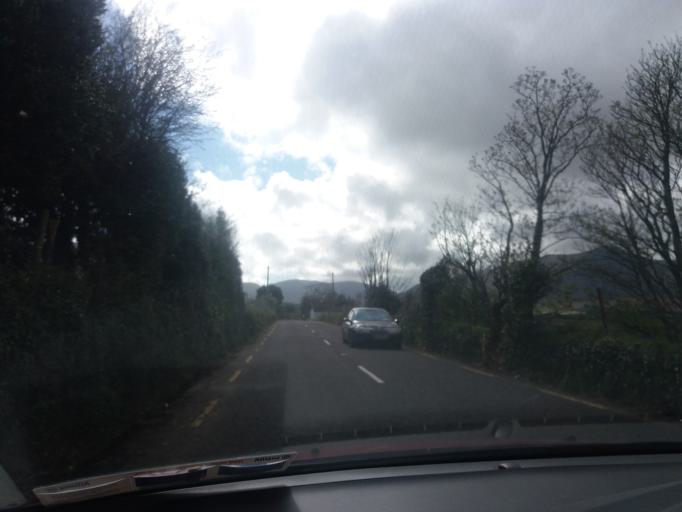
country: IE
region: Munster
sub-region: Ciarrai
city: Dingle
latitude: 52.2231
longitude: -10.1401
